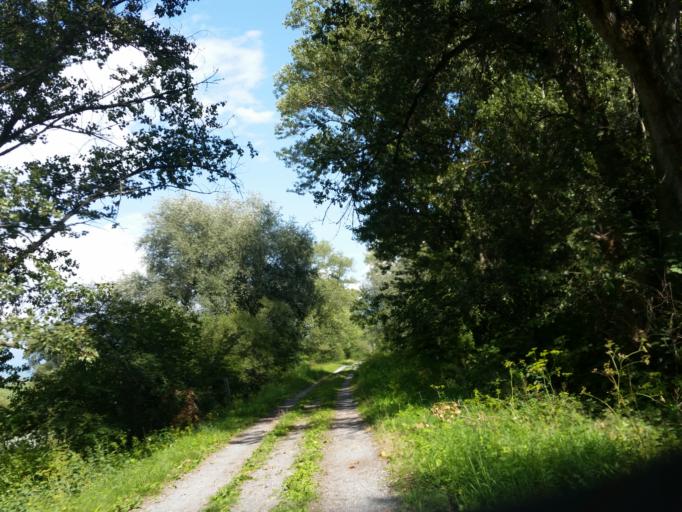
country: CH
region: Valais
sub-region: Martigny District
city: Leytron
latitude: 46.1772
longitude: 7.2076
